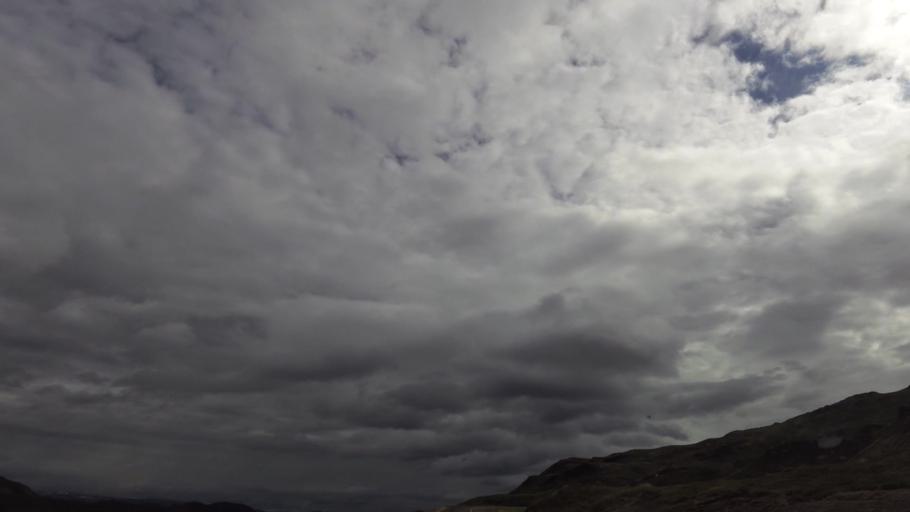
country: IS
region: West
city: Stykkisholmur
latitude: 65.5269
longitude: -22.1225
